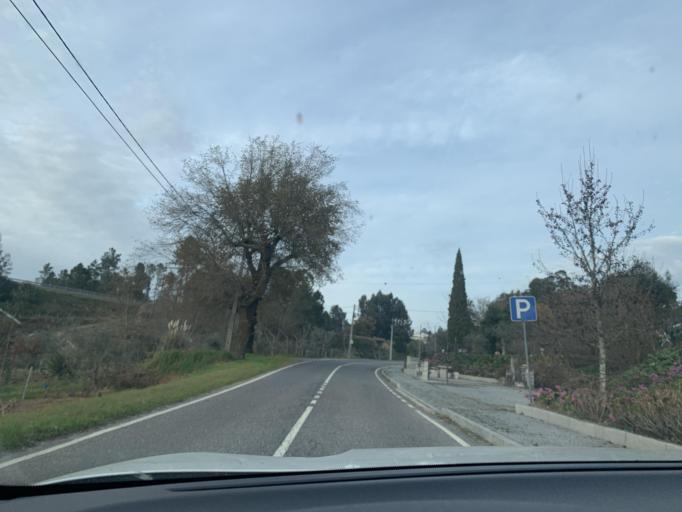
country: PT
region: Viseu
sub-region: Concelho de Tondela
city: Tondela
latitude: 40.5910
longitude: -8.0086
